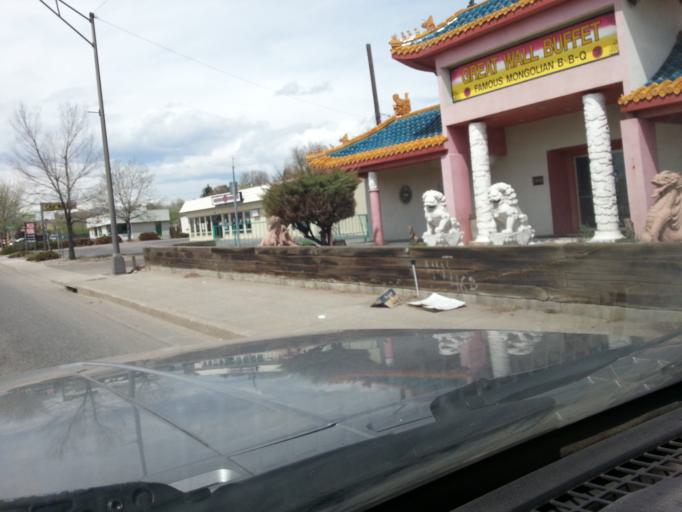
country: US
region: Colorado
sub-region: Larimer County
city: Loveland
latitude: 40.4073
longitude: -105.0995
